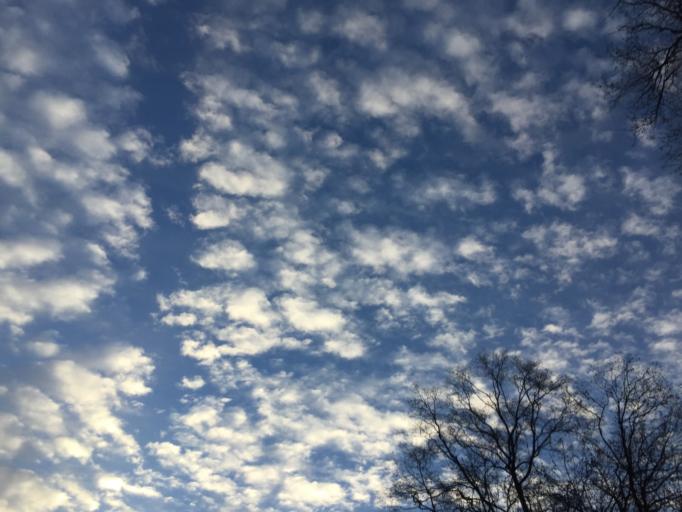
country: FR
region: Poitou-Charentes
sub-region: Departement de la Vienne
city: Coulombiers
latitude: 46.4661
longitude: 0.1912
